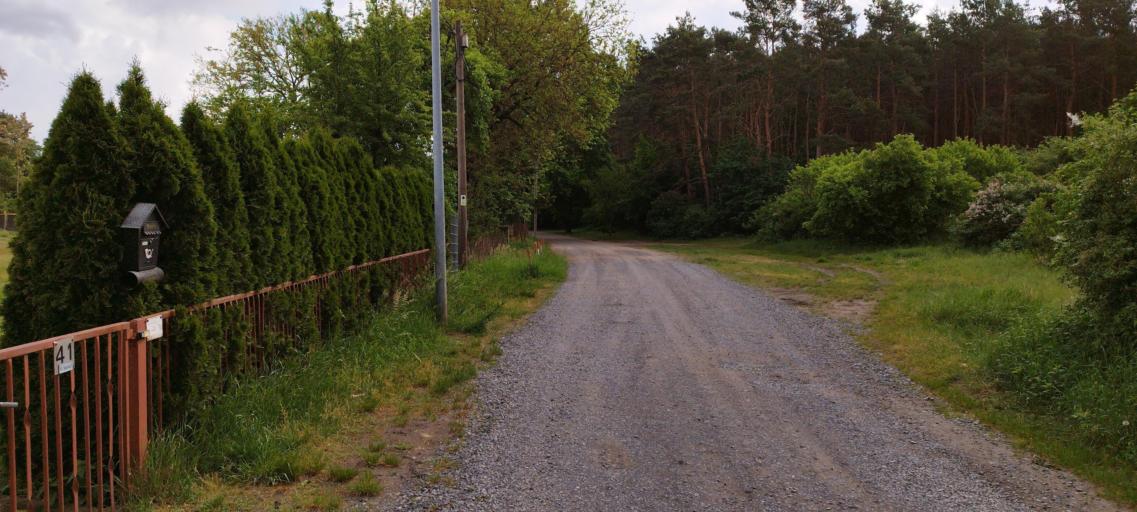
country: DE
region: Brandenburg
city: Furstenwalde
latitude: 52.3654
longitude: 14.0770
